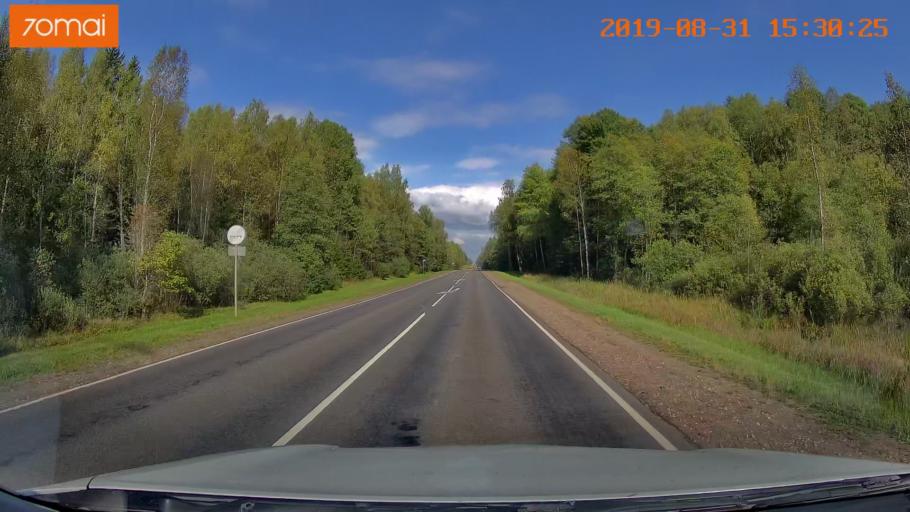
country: RU
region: Kaluga
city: Baryatino
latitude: 54.5755
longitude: 34.6296
